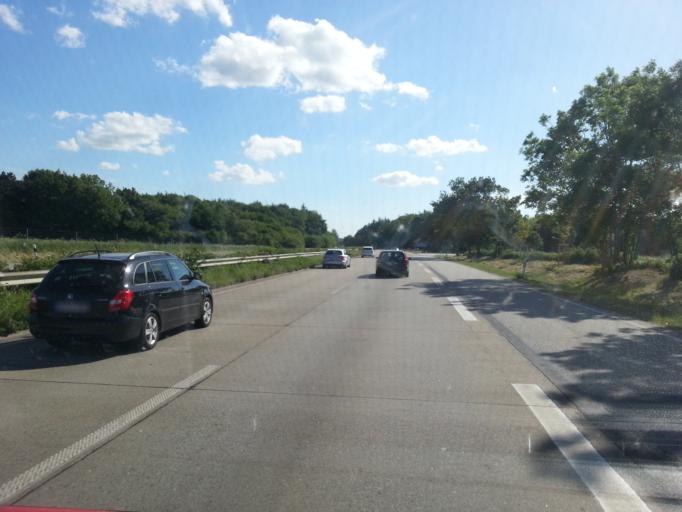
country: DE
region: Schleswig-Holstein
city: Susel
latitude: 54.0558
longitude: 10.7378
